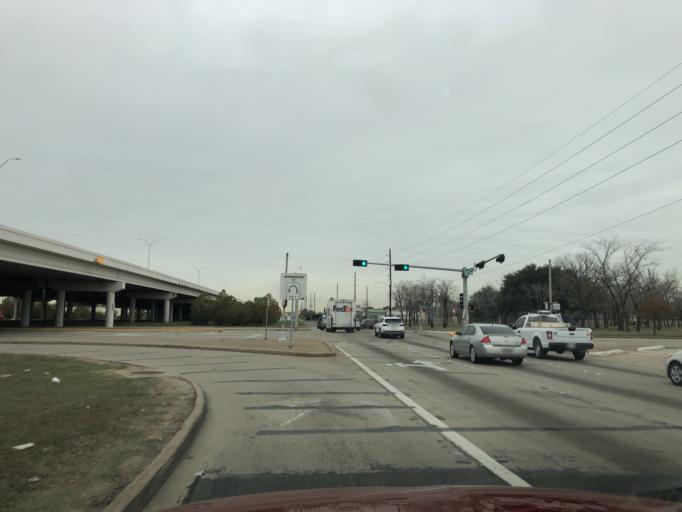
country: US
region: Texas
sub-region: Fort Bend County
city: Missouri City
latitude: 29.6441
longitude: -95.5383
